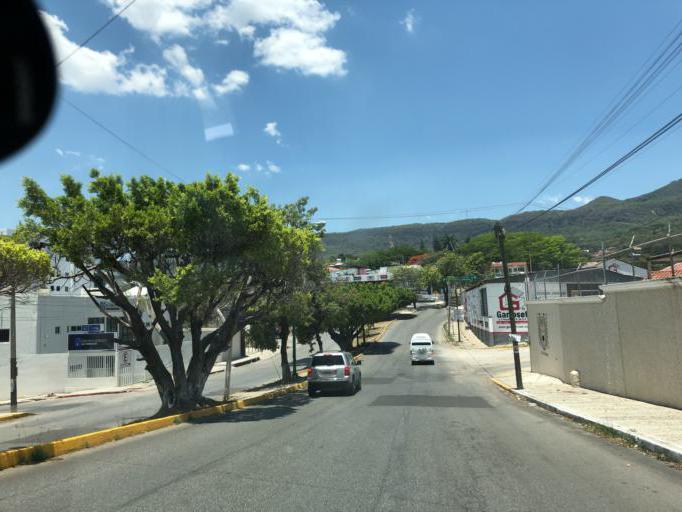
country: MX
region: Chiapas
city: Tuxtla Gutierrez
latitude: 16.7458
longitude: -93.1275
